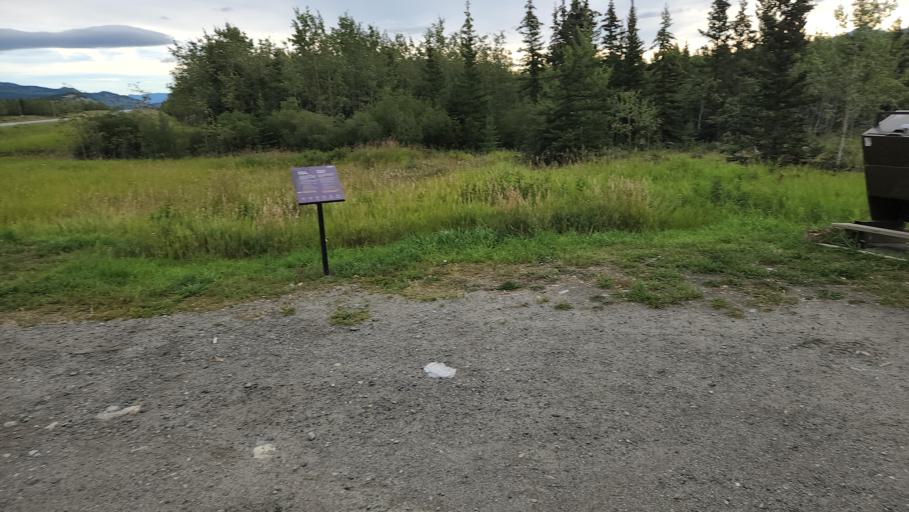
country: CA
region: Yukon
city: Whitehorse
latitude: 60.7842
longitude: -136.0244
